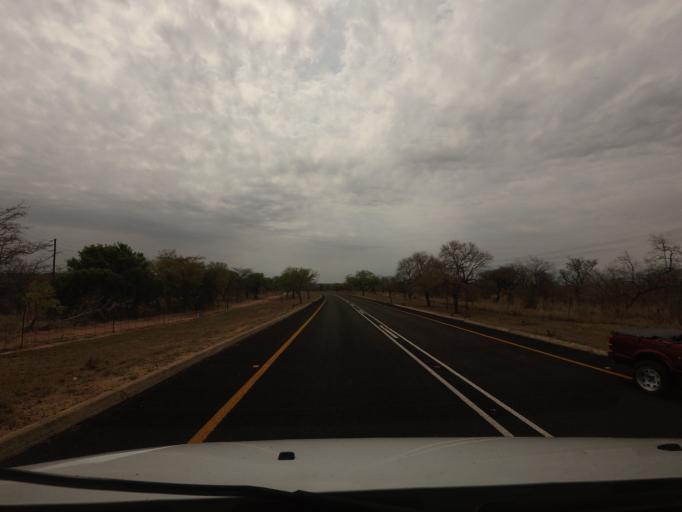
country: ZA
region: Limpopo
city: Thulamahashi
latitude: -24.5601
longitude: 31.1721
